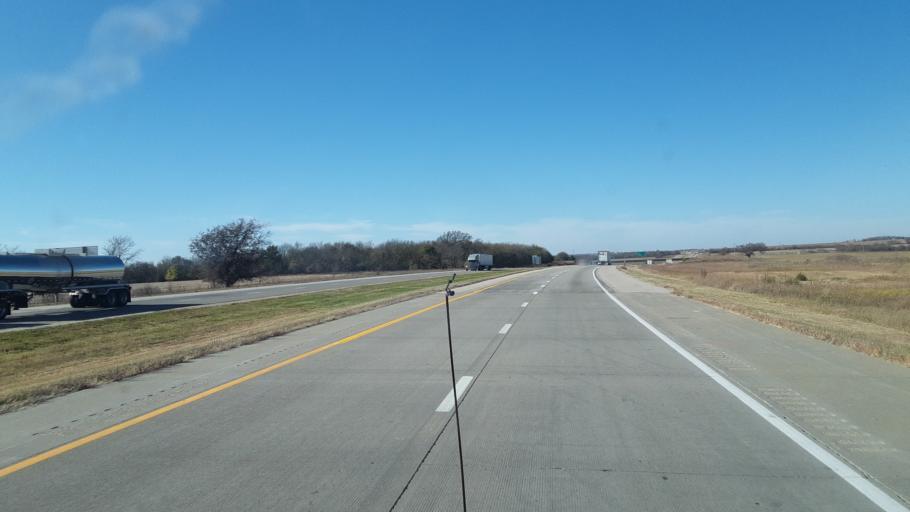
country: US
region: Kansas
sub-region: Osage County
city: Lyndon
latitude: 38.4264
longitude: -95.7402
